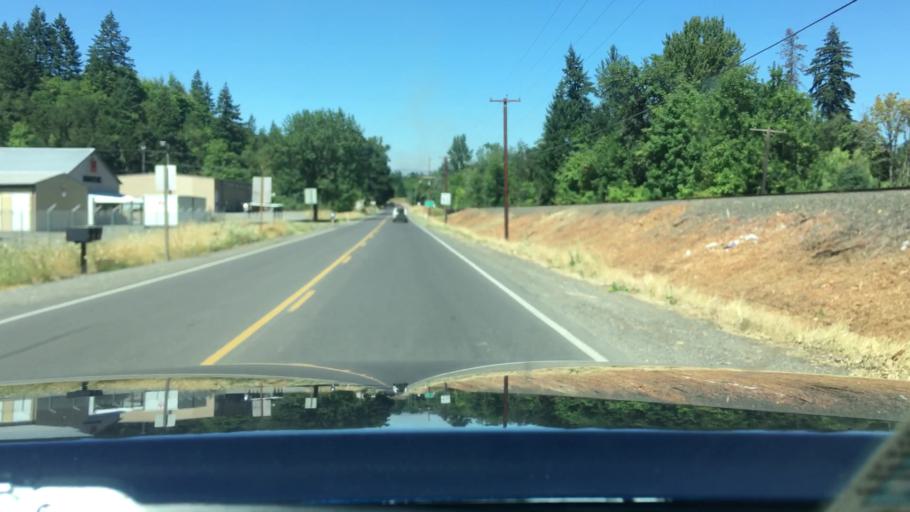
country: US
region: Oregon
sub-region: Lane County
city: Cottage Grove
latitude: 43.8091
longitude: -123.0497
